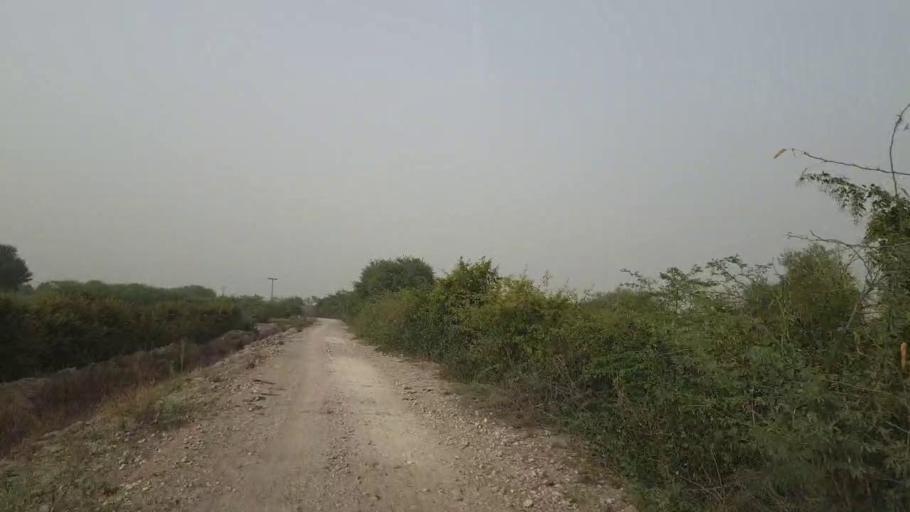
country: PK
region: Sindh
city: Kunri
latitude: 25.0683
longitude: 69.4879
